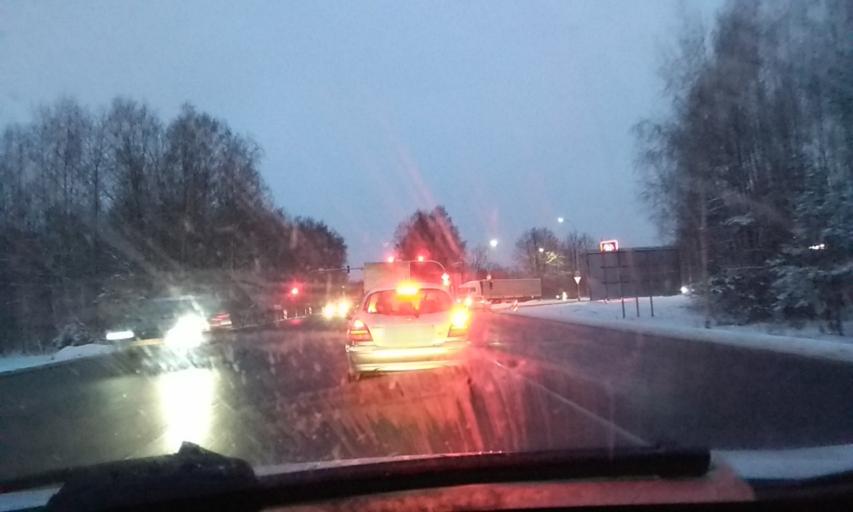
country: LT
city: Ramuciai
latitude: 54.9183
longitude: 24.0415
